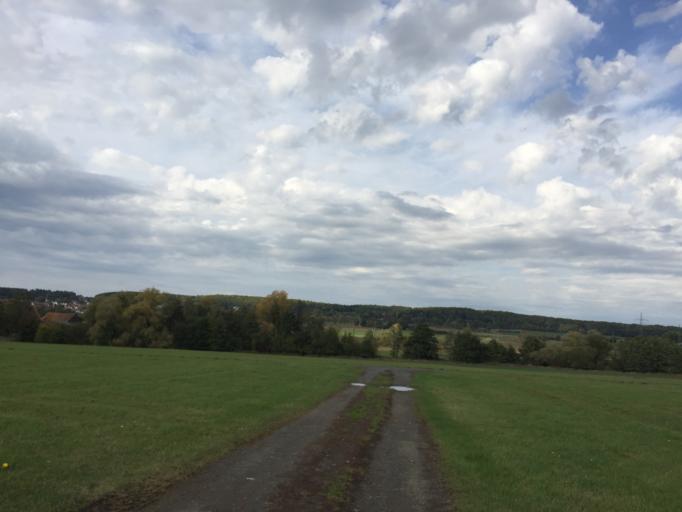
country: DE
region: Hesse
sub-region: Regierungsbezirk Giessen
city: Alten Buseck
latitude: 50.6080
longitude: 8.7655
